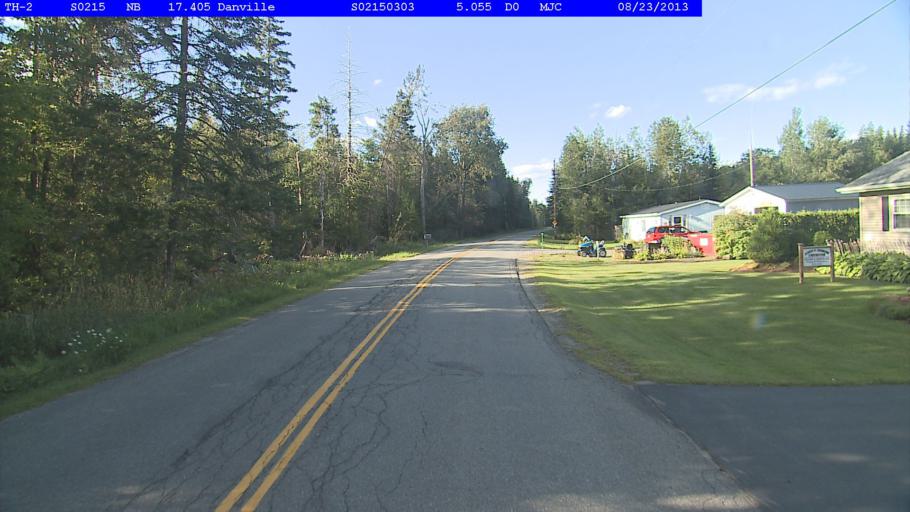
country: US
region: Vermont
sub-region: Caledonia County
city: St Johnsbury
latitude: 44.4366
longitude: -72.1424
